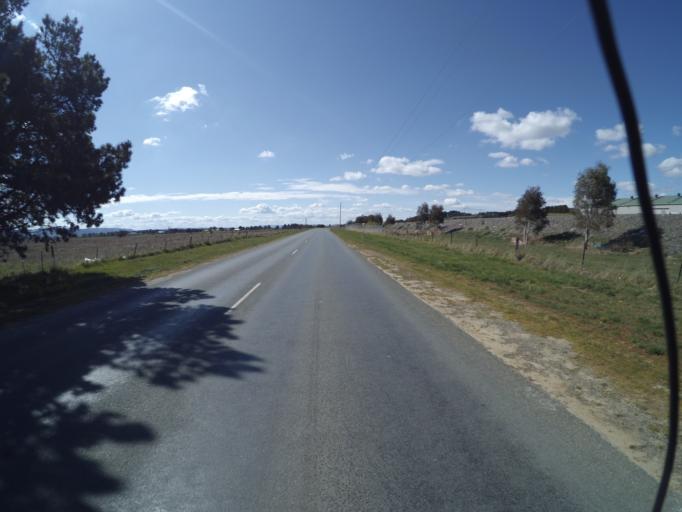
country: AU
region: New South Wales
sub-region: Palerang
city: Bungendore
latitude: -35.2372
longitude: 149.4443
